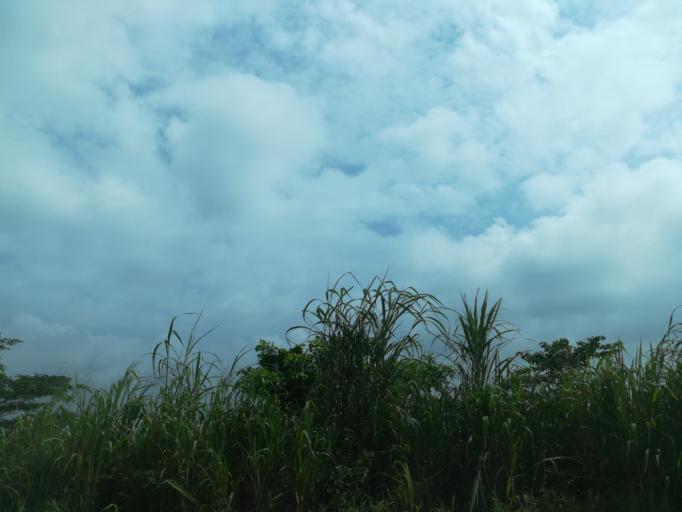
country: NG
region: Lagos
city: Ikorodu
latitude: 6.6738
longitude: 3.6555
